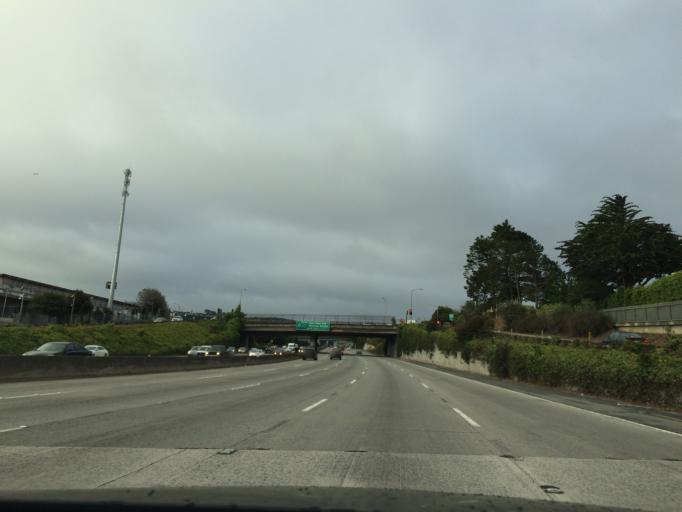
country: US
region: California
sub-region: San Mateo County
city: Daly City
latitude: 37.7227
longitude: -122.4480
